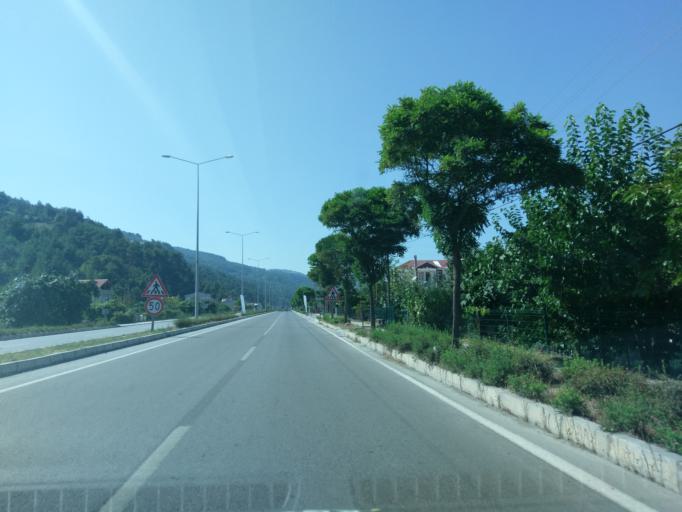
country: TR
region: Samsun
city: Yakakent
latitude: 41.6428
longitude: 35.4870
